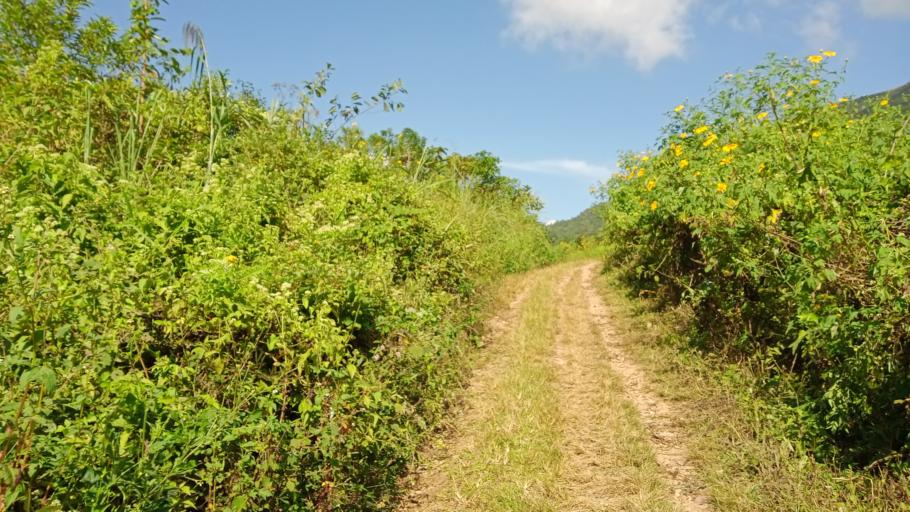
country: LA
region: Xiangkhoang
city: Phonsavan
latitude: 19.1096
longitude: 102.9305
